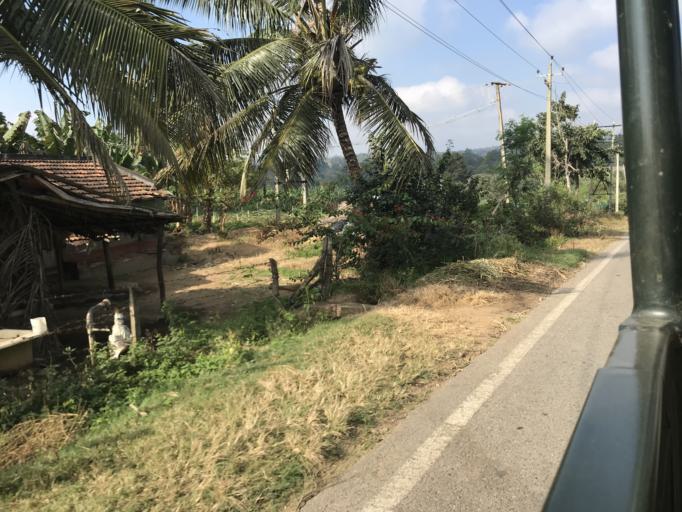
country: IN
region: Karnataka
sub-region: Mysore
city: Heggadadevankote
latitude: 11.9471
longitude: 76.2514
